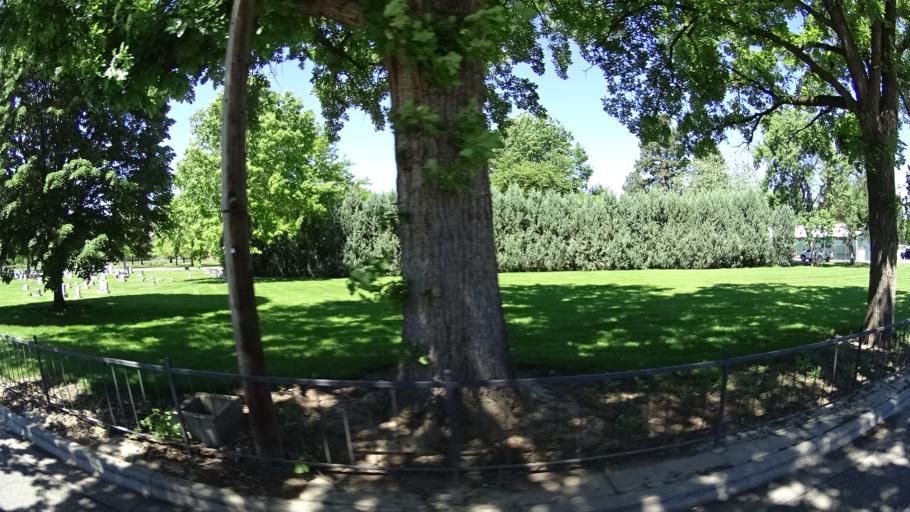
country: US
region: Idaho
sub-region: Ada County
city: Garden City
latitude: 43.6068
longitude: -116.2286
